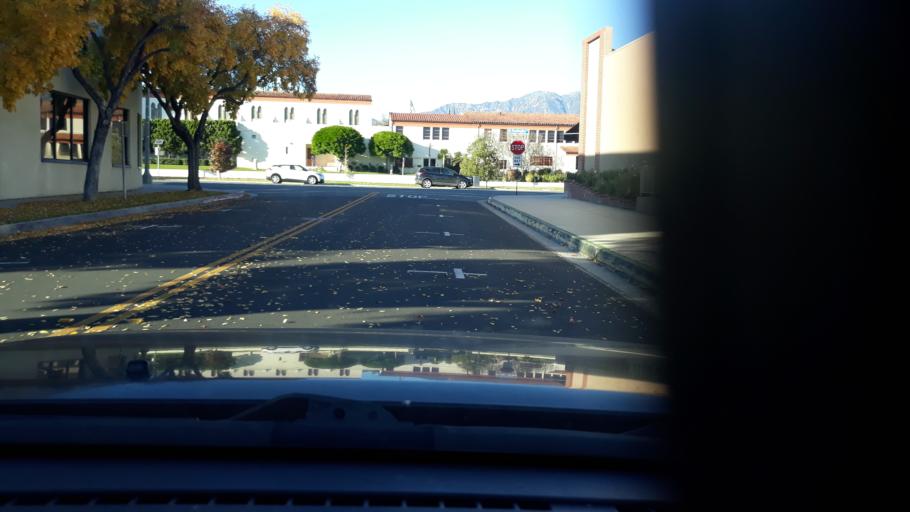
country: US
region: California
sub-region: Los Angeles County
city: San Marino
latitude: 34.1261
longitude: -118.0920
